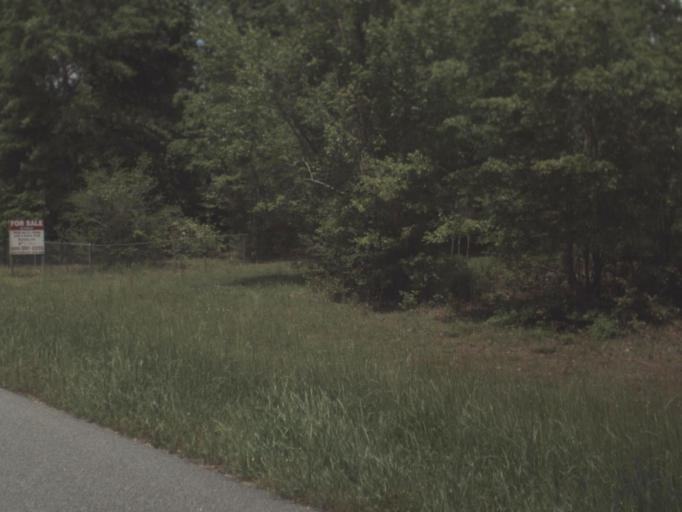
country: US
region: Florida
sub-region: Escambia County
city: Molino
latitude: 30.7738
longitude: -87.3942
